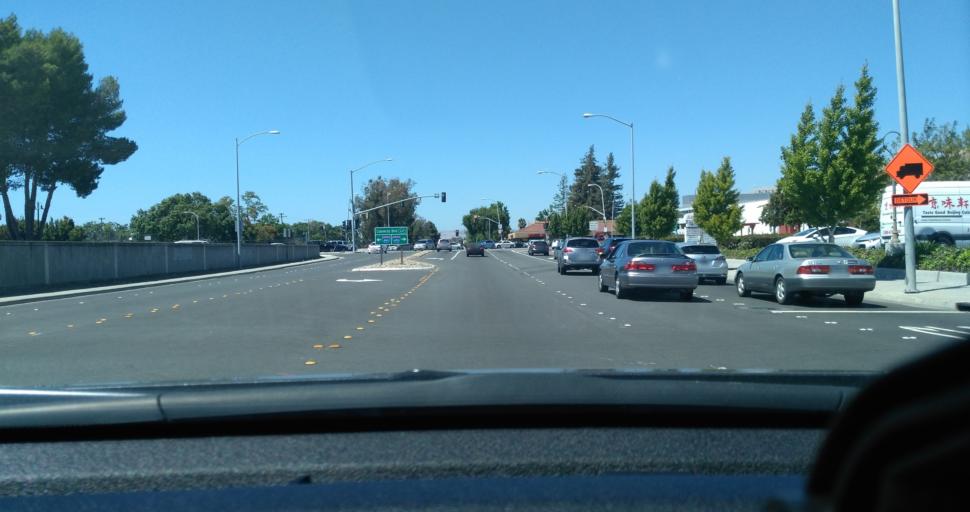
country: US
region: California
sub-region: Santa Clara County
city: Milpitas
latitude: 37.4290
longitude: -121.9086
